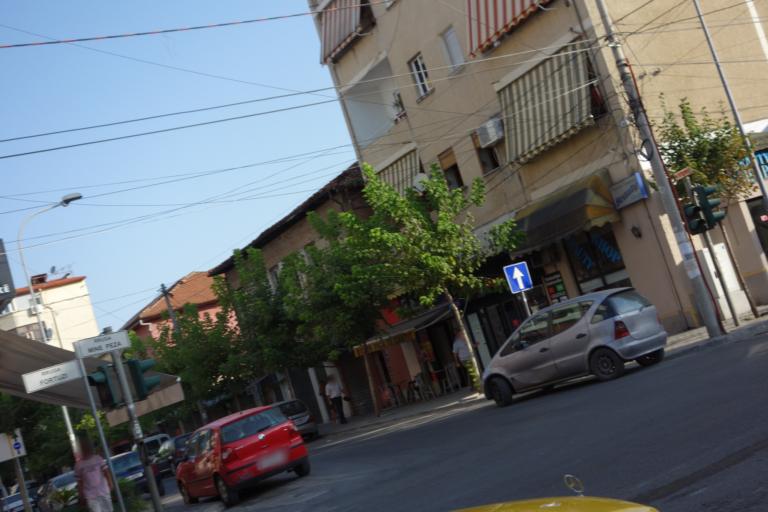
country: AL
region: Tirane
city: Tirana
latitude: 41.3309
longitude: 19.8126
